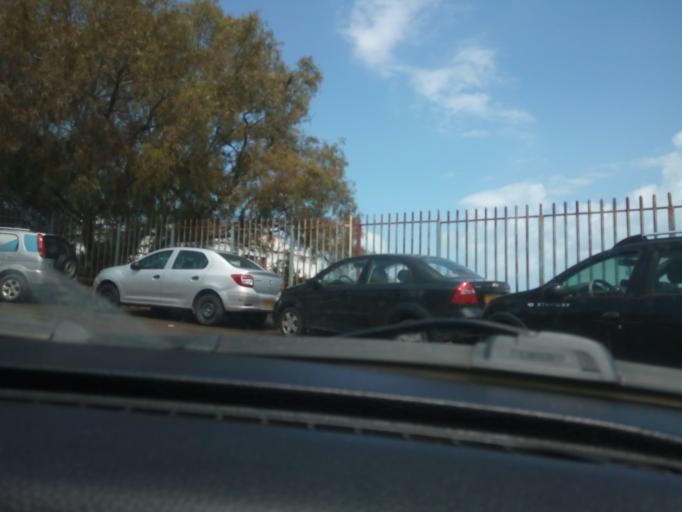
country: DZ
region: Alger
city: Algiers
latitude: 36.7882
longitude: 3.0566
